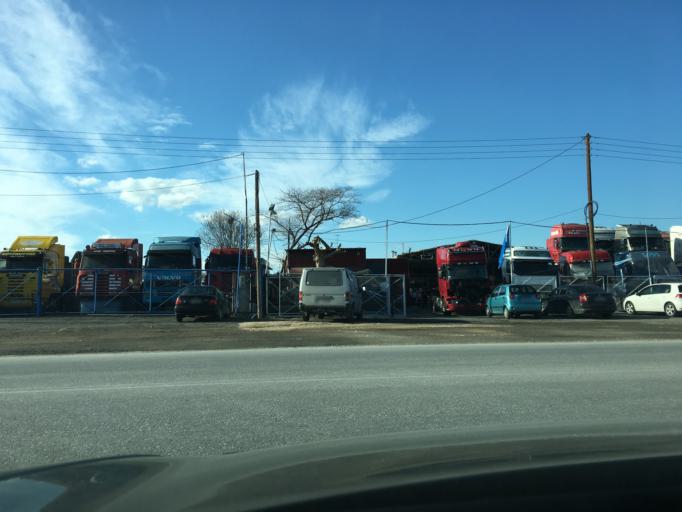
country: GR
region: Thessaly
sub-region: Nomos Larisis
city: Larisa
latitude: 39.6359
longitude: 22.4360
